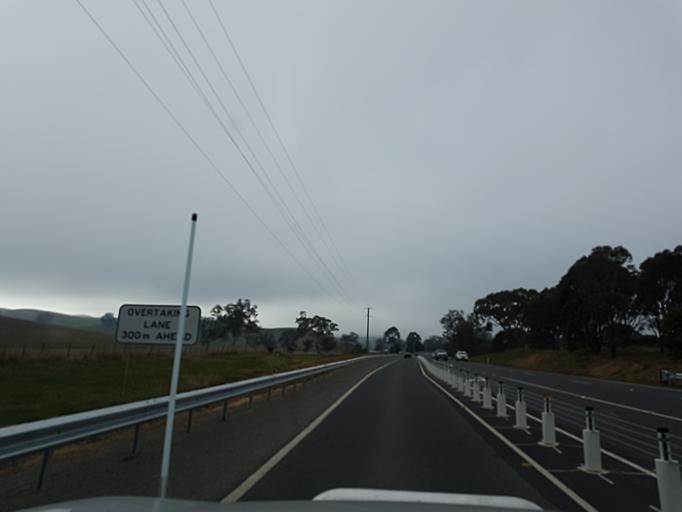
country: AU
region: Victoria
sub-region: Murrindindi
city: Alexandra
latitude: -37.2036
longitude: 145.4628
